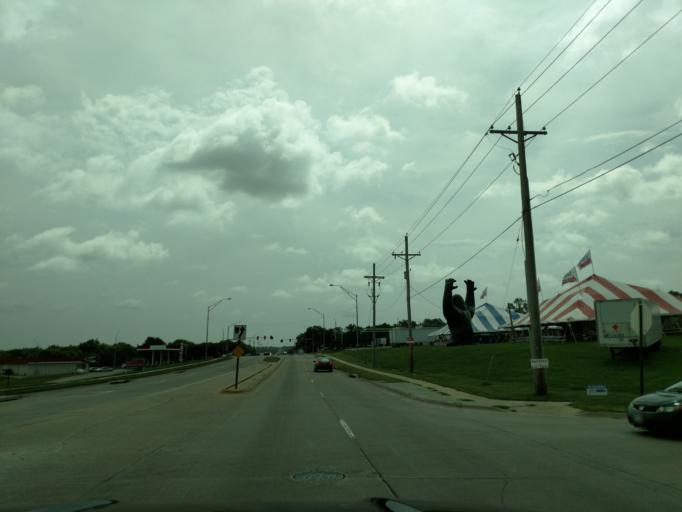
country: US
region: Nebraska
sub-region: Sarpy County
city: La Vista
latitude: 41.1907
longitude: -96.0263
